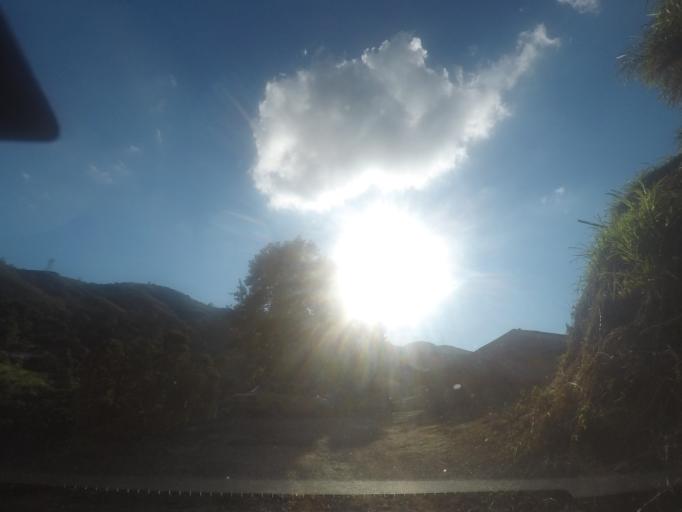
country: BR
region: Rio de Janeiro
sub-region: Petropolis
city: Petropolis
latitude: -22.5002
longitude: -43.1436
